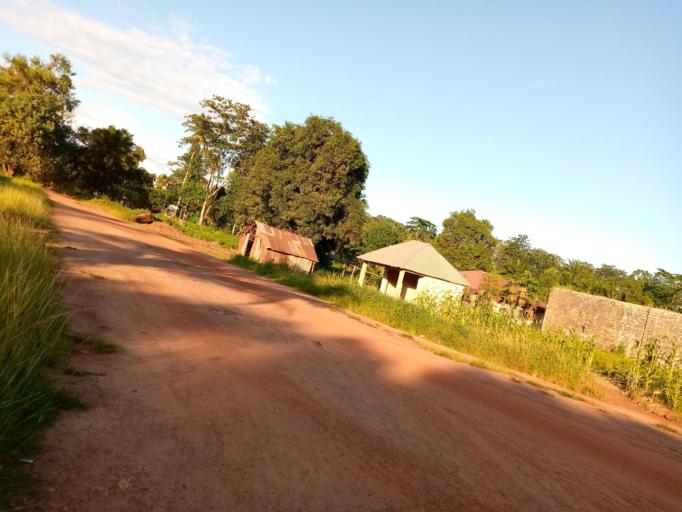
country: SL
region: Northern Province
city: Yonibana
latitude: 8.4437
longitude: -12.2392
